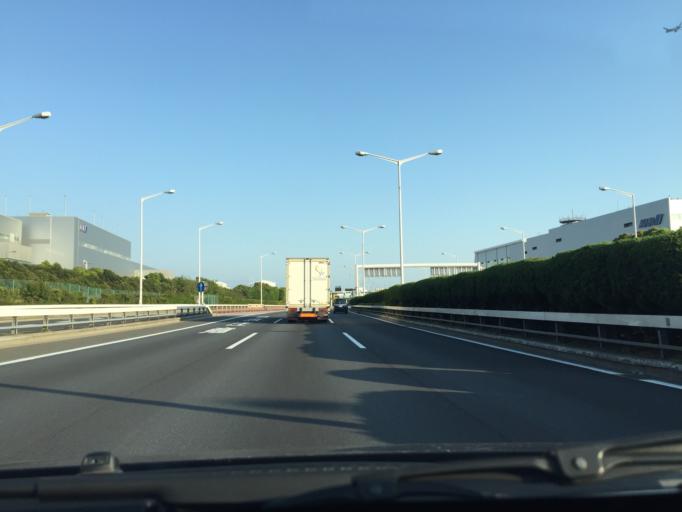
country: JP
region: Kanagawa
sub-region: Kawasaki-shi
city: Kawasaki
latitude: 35.5397
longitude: 139.7936
